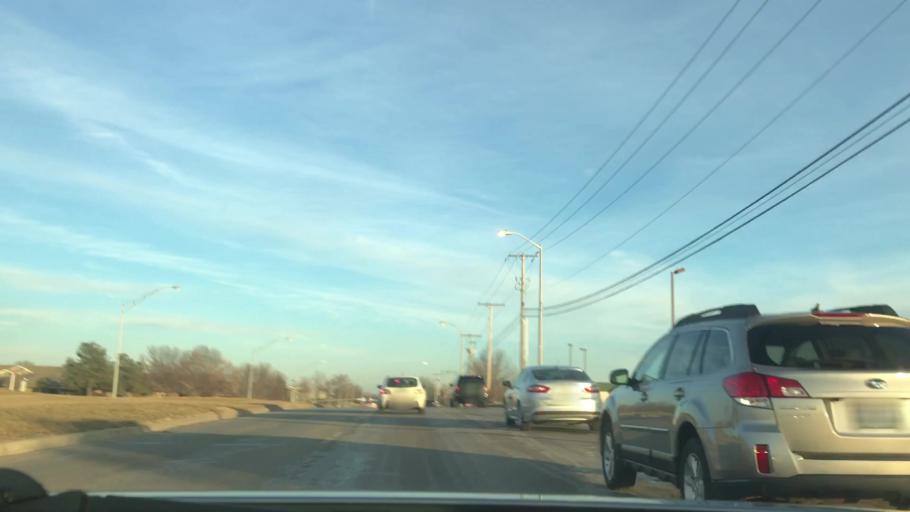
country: US
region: Missouri
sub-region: Platte County
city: Weatherby Lake
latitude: 39.2468
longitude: -94.6503
